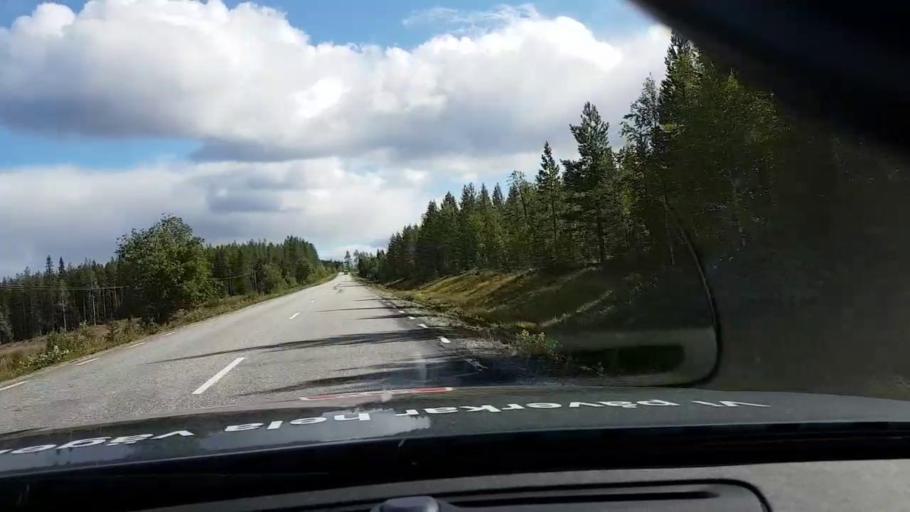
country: SE
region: Vaesterbotten
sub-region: Asele Kommun
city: Asele
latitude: 63.7758
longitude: 17.6724
